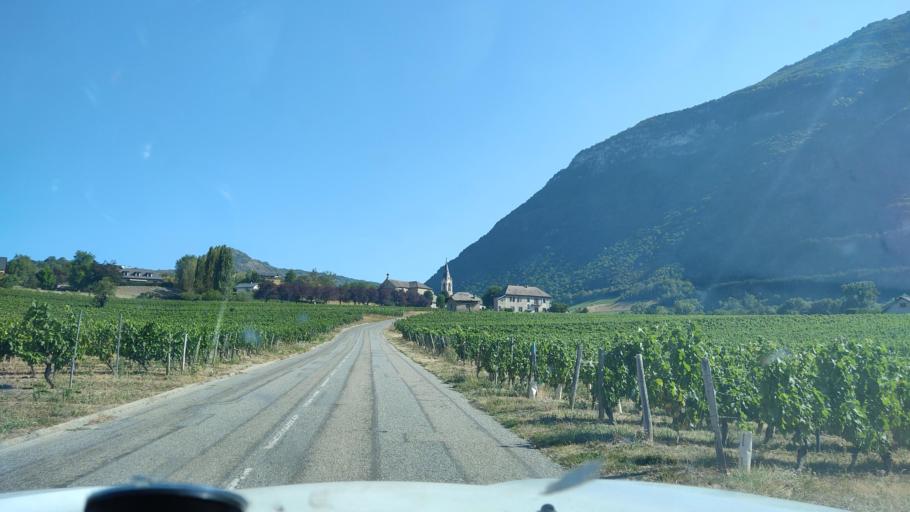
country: FR
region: Rhone-Alpes
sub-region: Departement de la Savoie
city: Les Marches
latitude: 45.5227
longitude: 6.0058
